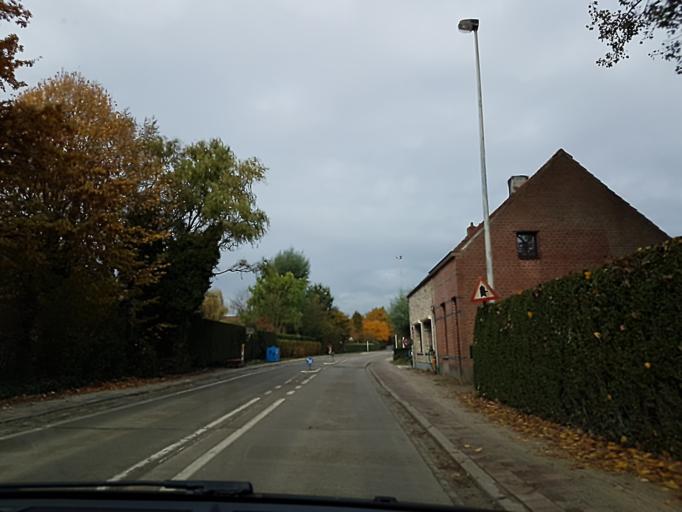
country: BE
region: Flanders
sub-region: Provincie Antwerpen
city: Boechout
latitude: 51.1464
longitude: 4.4852
